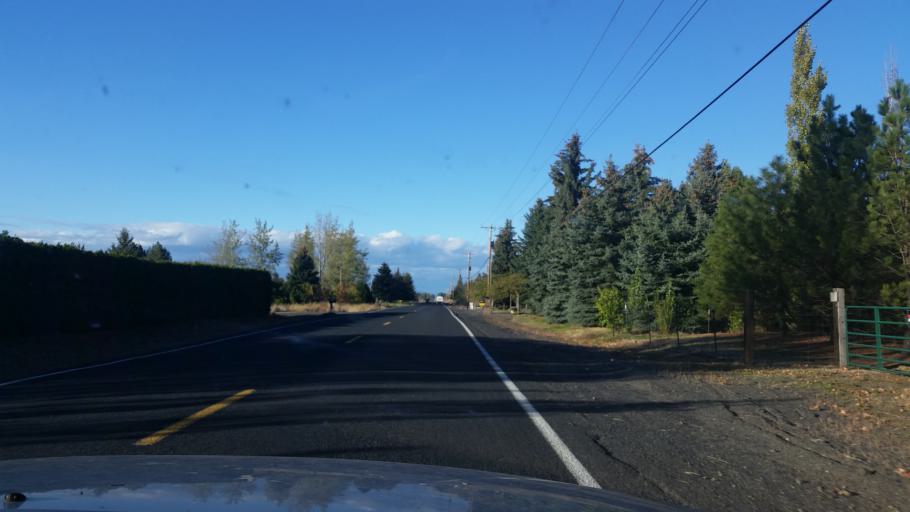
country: US
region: Washington
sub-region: Spokane County
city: Fairchild Air Force Base
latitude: 47.5876
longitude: -117.6075
